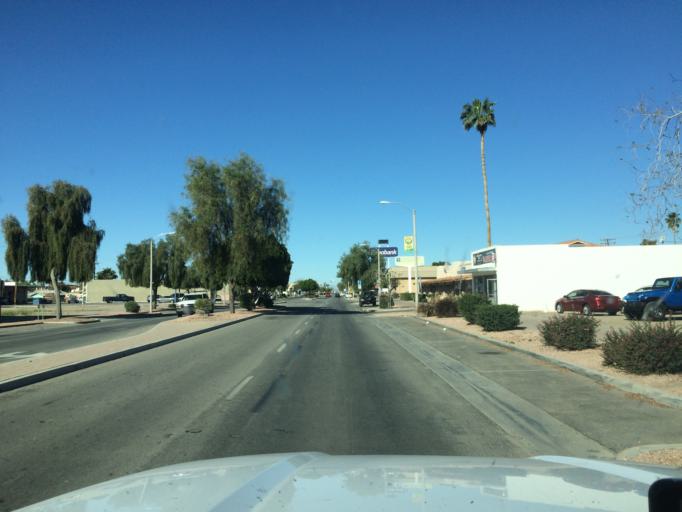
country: US
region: California
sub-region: Riverside County
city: Blythe
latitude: 33.6105
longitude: -114.5942
